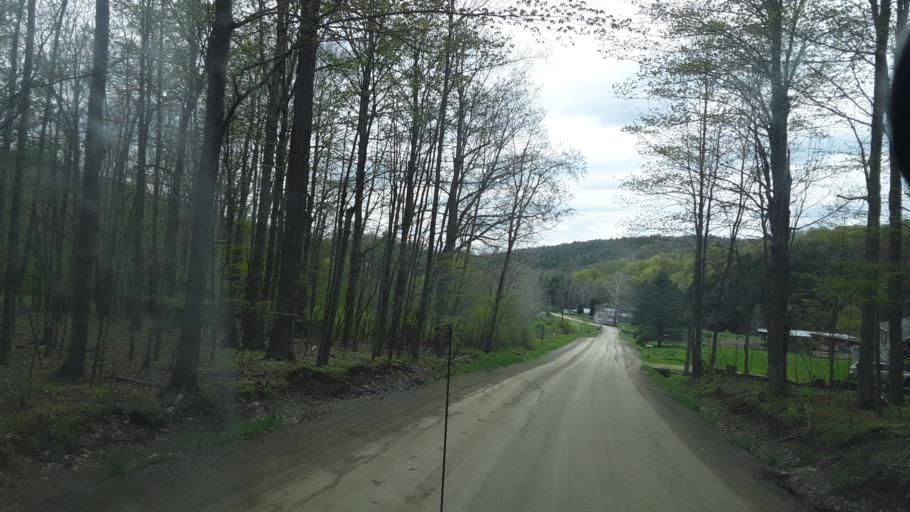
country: US
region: New York
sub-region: Steuben County
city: Addison
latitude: 42.1015
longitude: -77.3379
